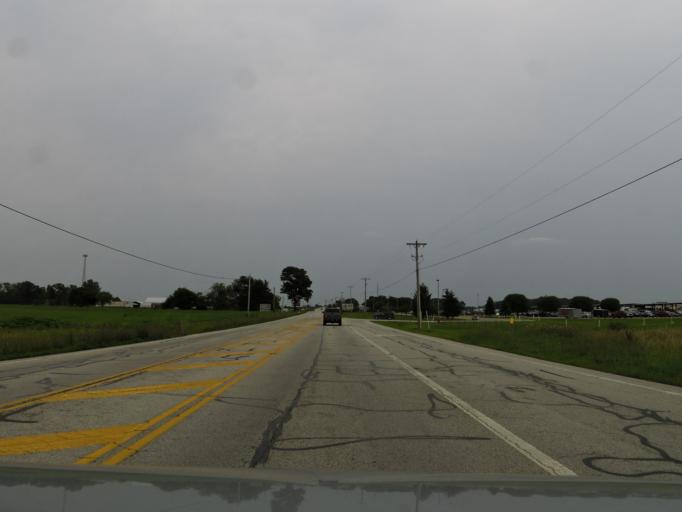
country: US
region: Ohio
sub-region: Clinton County
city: Wilmington
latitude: 39.4877
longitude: -83.9529
